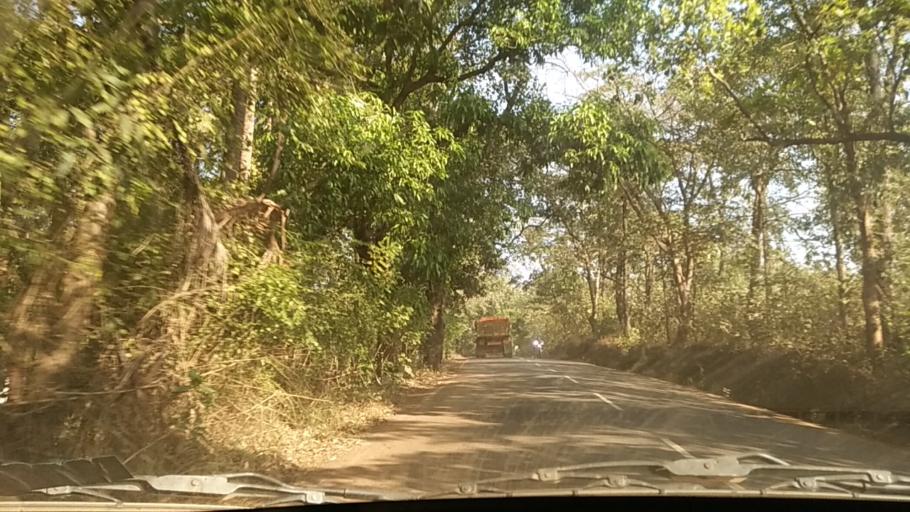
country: IN
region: Goa
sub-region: South Goa
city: Sanvordem
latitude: 15.2982
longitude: 74.1354
